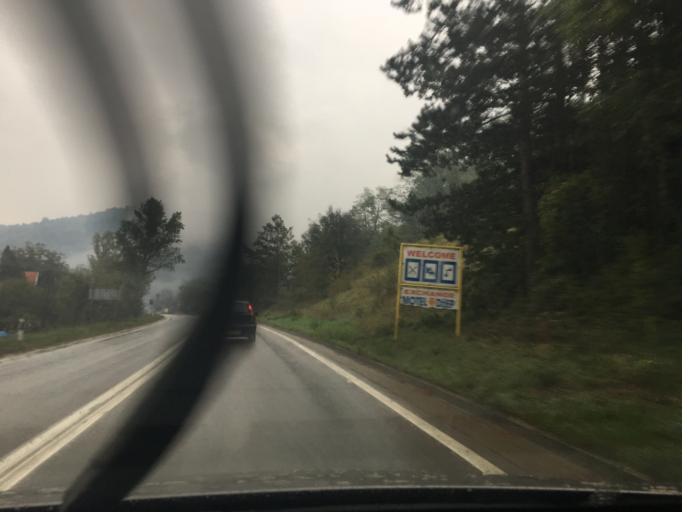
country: RS
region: Central Serbia
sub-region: Pcinjski Okrug
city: Vladicin Han
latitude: 42.7726
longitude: 22.0904
